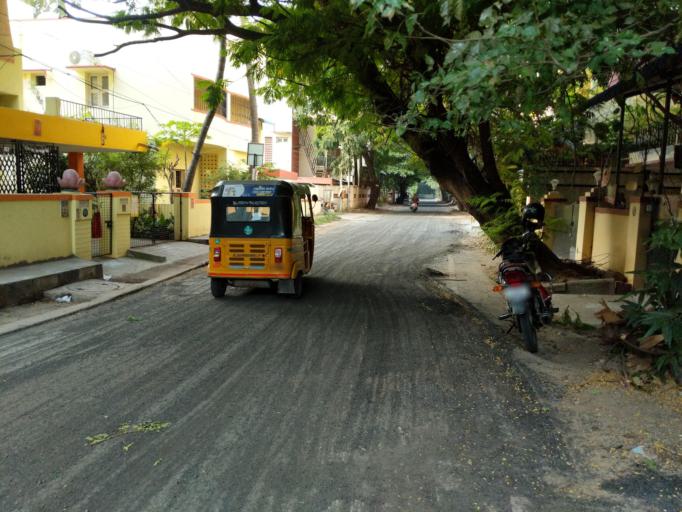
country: IN
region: Tamil Nadu
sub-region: Chennai
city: Gandhi Nagar
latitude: 13.0051
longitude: 80.2607
